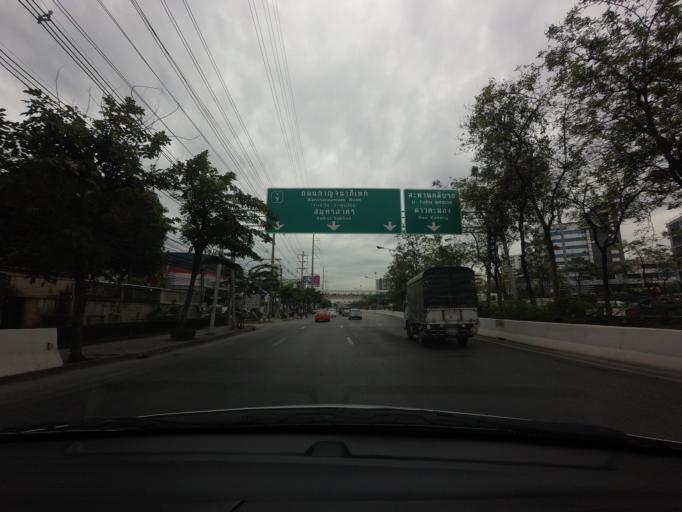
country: TH
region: Bangkok
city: Chom Thong
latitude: 13.6769
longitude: 100.4639
